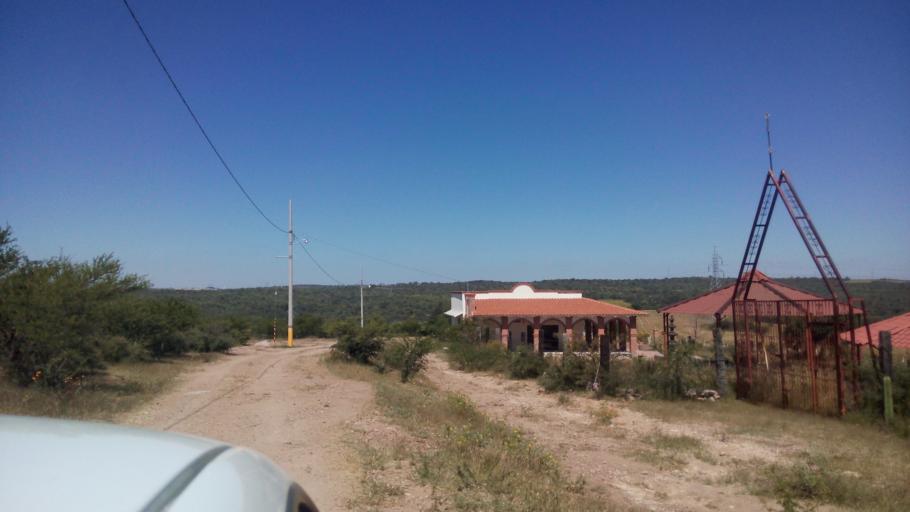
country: MX
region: Aguascalientes
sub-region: Aguascalientes
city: San Sebastian [Fraccionamiento]
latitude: 21.7980
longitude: -102.2353
